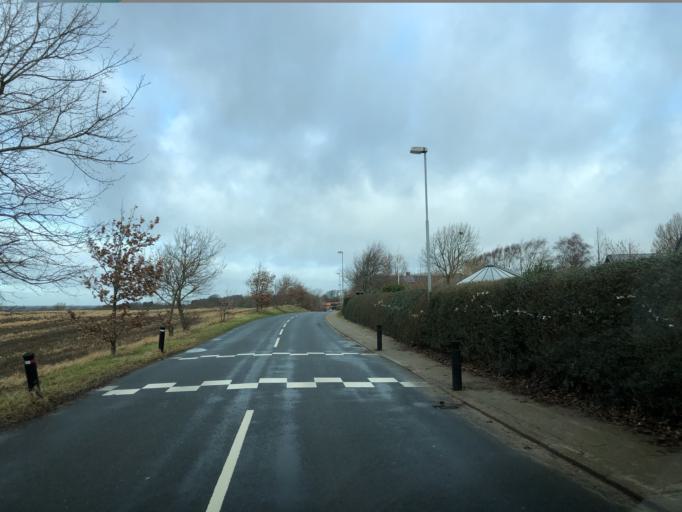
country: DK
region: Central Jutland
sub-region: Skive Kommune
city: Skive
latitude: 56.4373
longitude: 9.0088
